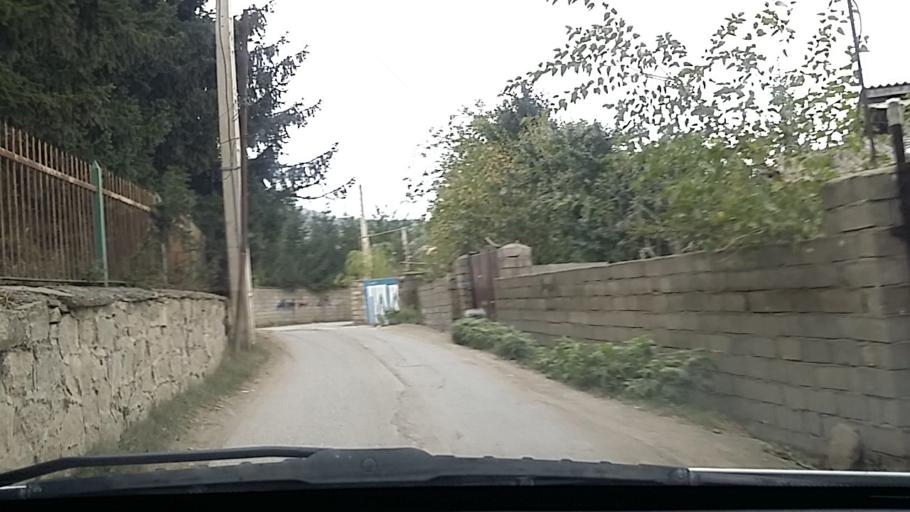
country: IR
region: Mazandaran
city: `Abbasabad
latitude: 36.5107
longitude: 51.1615
